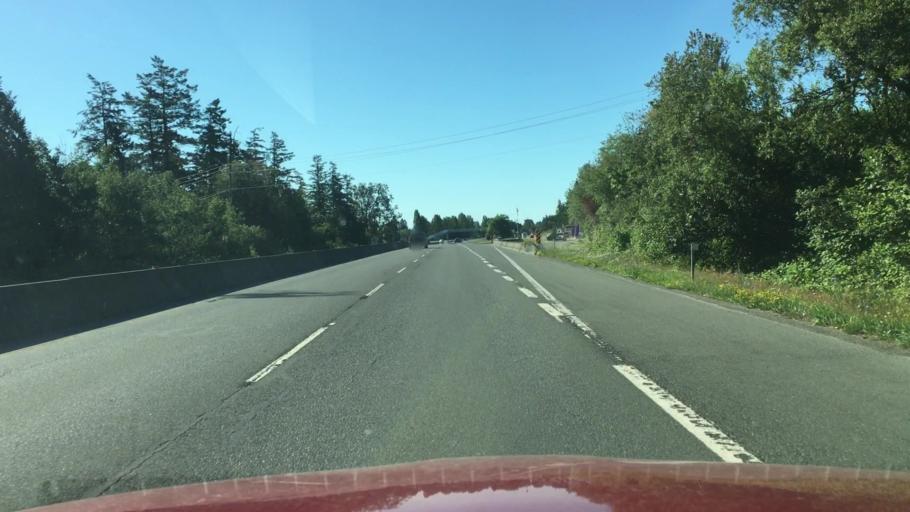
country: CA
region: British Columbia
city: North Saanich
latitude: 48.6668
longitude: -123.4220
